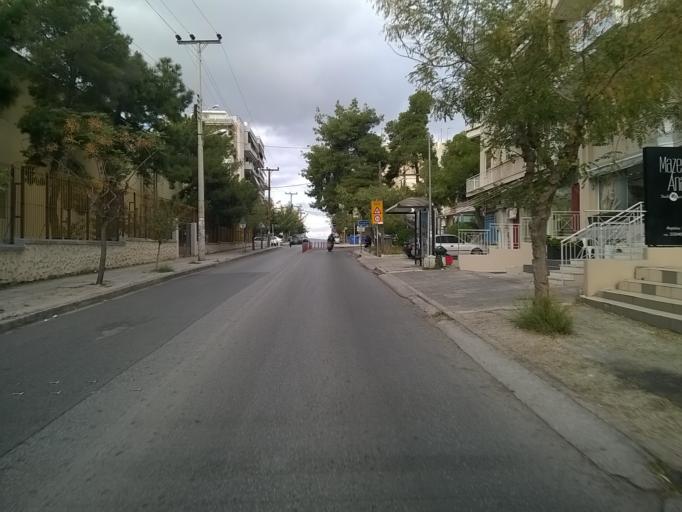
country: GR
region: Attica
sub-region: Nomarchia Athinas
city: Nea Smyrni
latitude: 37.9473
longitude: 23.7232
